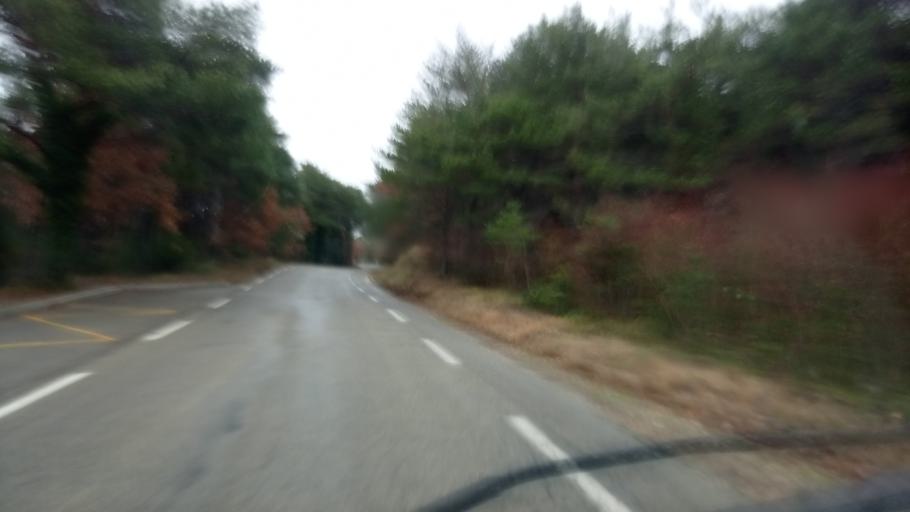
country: FR
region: Provence-Alpes-Cote d'Azur
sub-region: Departement du Var
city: Ginasservis
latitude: 43.7077
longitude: 5.8679
